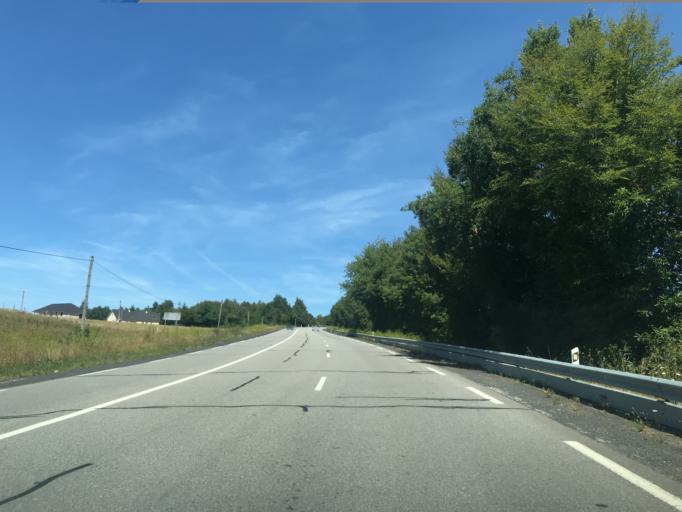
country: FR
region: Limousin
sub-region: Departement de la Correze
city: Naves
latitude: 45.2986
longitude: 1.8151
